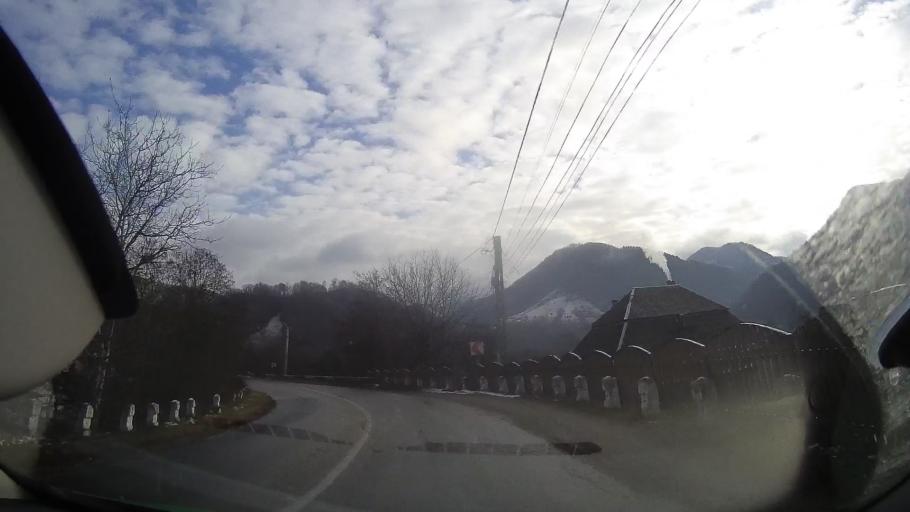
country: RO
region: Alba
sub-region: Comuna Lupsa
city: Lupsa
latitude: 46.3805
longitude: 23.2294
